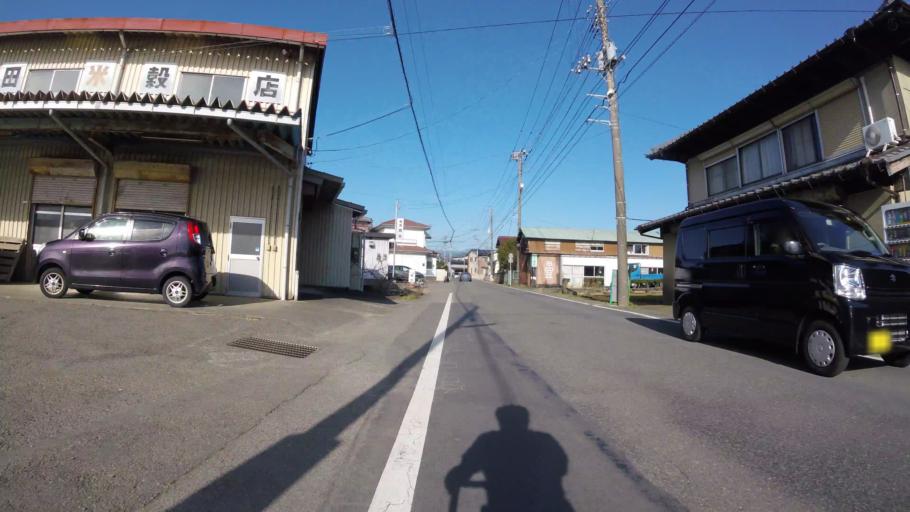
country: JP
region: Shizuoka
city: Mishima
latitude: 35.0558
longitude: 138.9538
